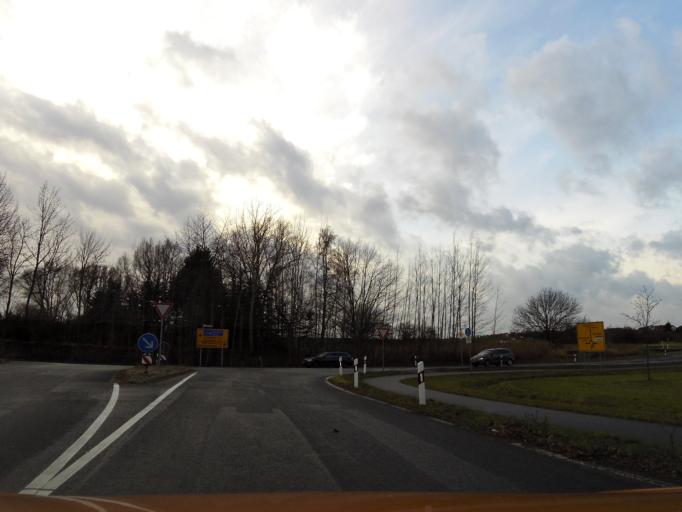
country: DE
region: Lower Saxony
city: Wolfsburg
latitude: 52.3930
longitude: 10.8462
